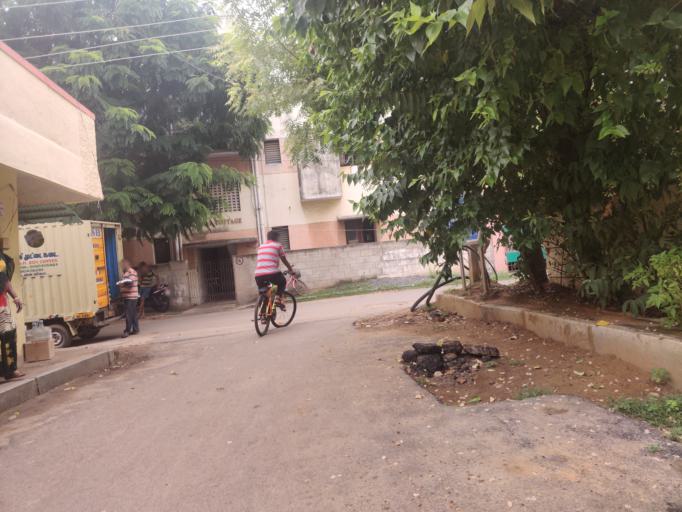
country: IN
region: Tamil Nadu
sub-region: Thiruvallur
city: Chinnasekkadu
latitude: 13.1227
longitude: 80.2190
